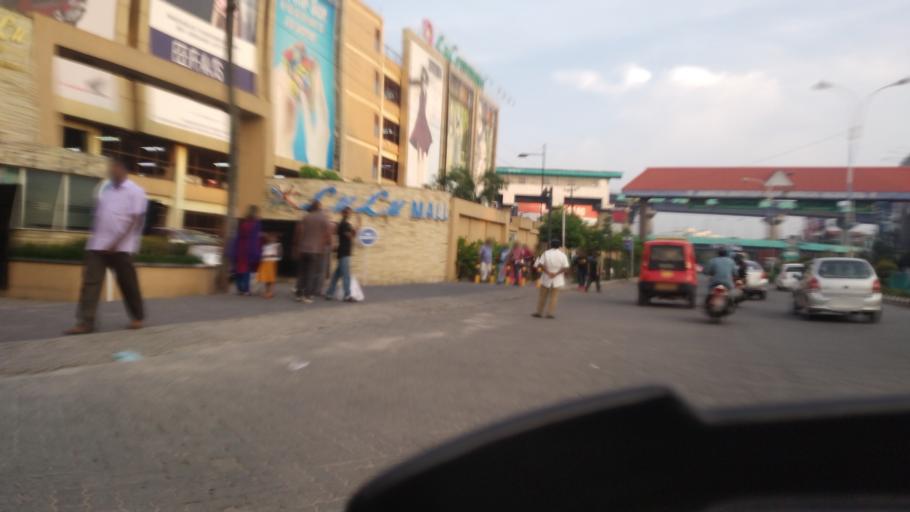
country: IN
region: Kerala
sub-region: Ernakulam
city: Elur
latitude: 10.0260
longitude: 76.3068
